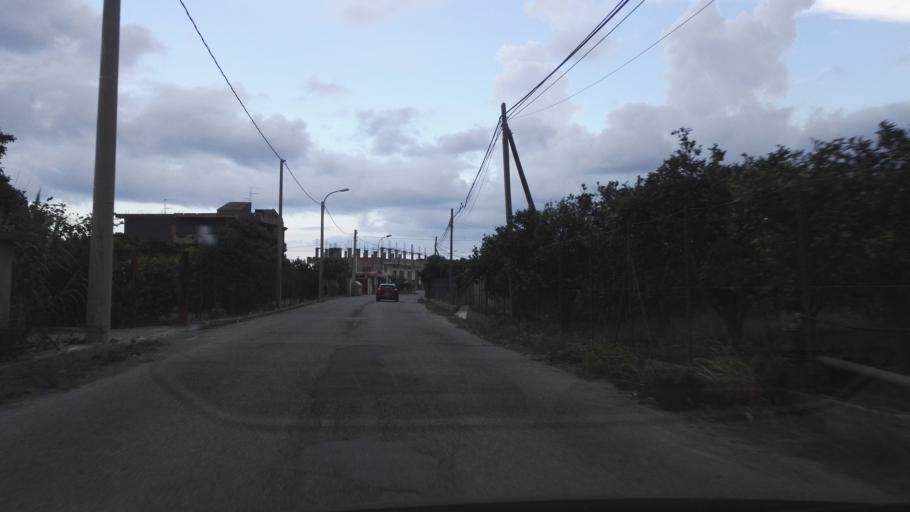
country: IT
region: Calabria
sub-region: Provincia di Reggio Calabria
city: Caulonia Marina
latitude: 38.3524
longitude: 16.4724
